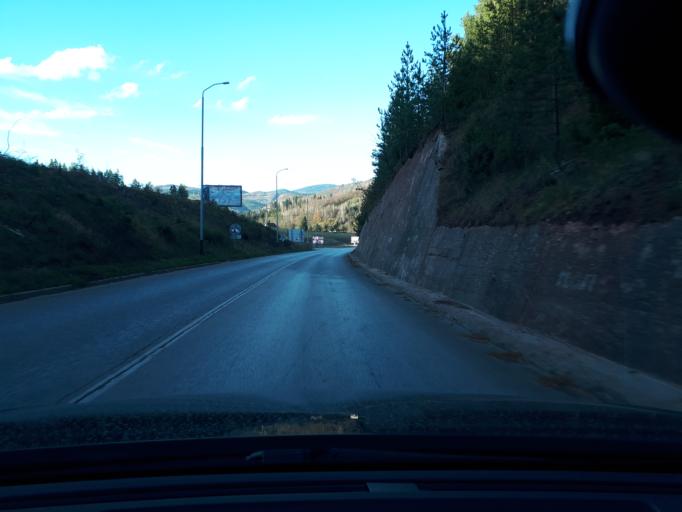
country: BA
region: Republika Srpska
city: Pale
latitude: 43.8312
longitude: 18.5580
